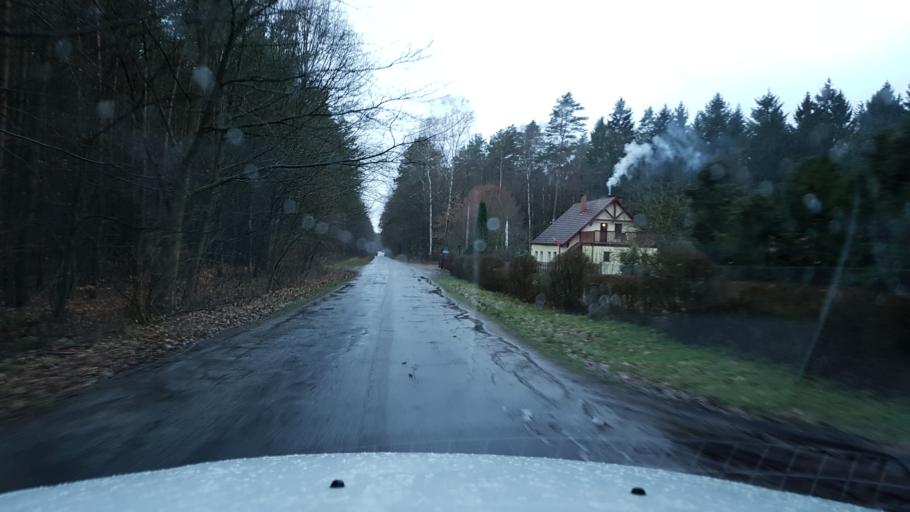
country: PL
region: West Pomeranian Voivodeship
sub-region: Powiat goleniowski
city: Mosty
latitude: 53.5586
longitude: 14.9878
